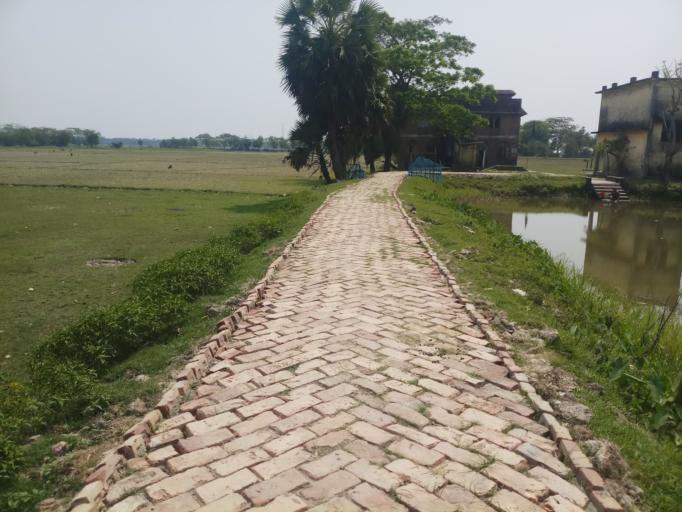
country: BD
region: Barisal
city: Mathba
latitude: 22.0424
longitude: 90.2842
